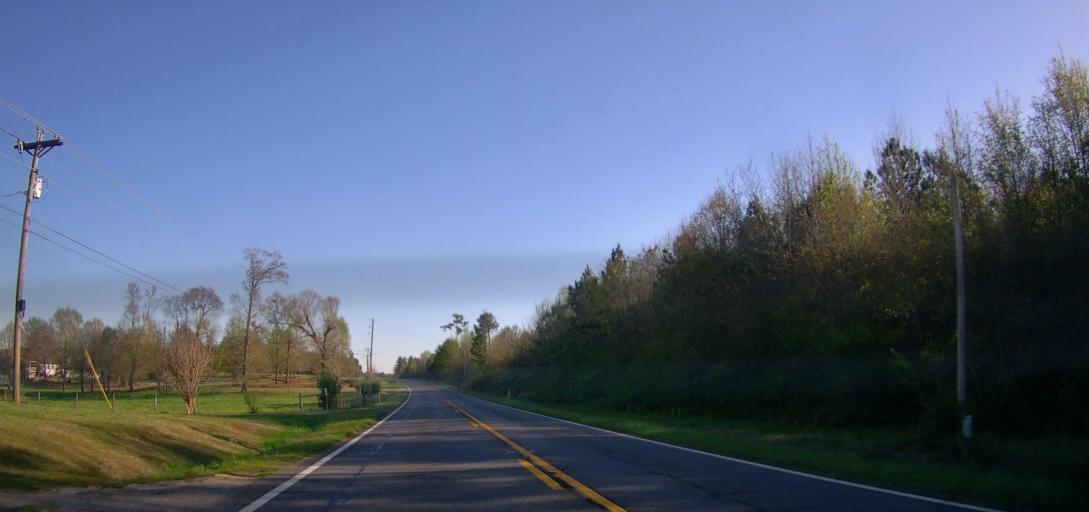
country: US
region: Georgia
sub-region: Butts County
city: Indian Springs
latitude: 33.1713
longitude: -83.9584
